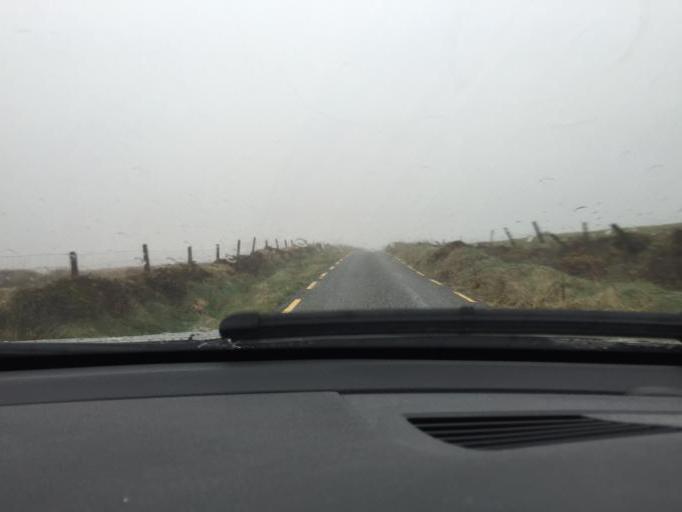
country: IE
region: Munster
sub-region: Ciarrai
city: Dingle
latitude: 52.1382
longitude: -10.4387
